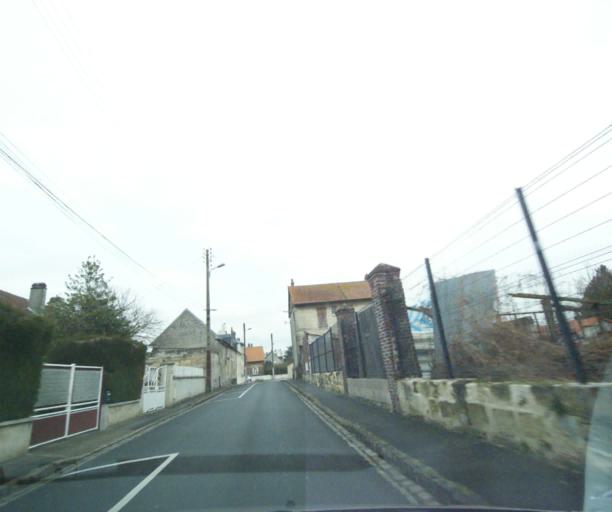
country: FR
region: Picardie
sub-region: Departement de l'Oise
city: Noyon
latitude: 49.5768
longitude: 2.9897
